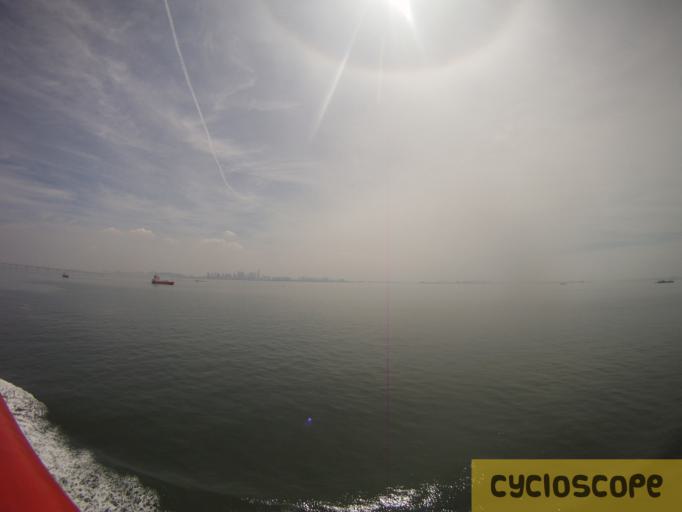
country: KR
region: Incheon
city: Incheon
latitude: 37.3976
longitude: 126.5569
